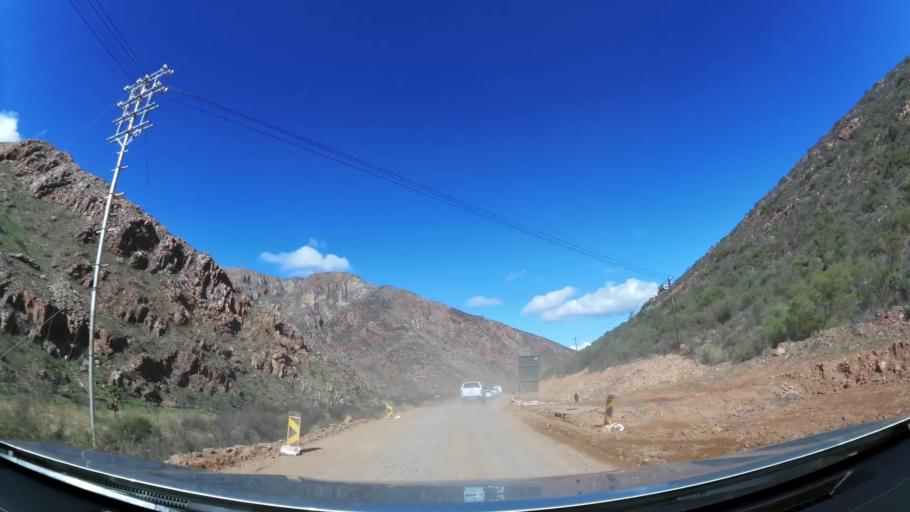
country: ZA
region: Western Cape
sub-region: Cape Winelands District Municipality
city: Ashton
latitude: -33.8058
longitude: 20.0941
